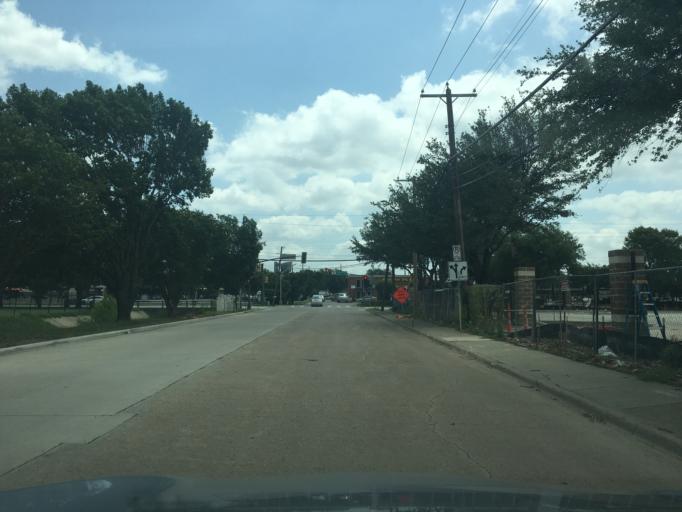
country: US
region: Texas
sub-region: Dallas County
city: Addison
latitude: 32.9143
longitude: -96.8194
